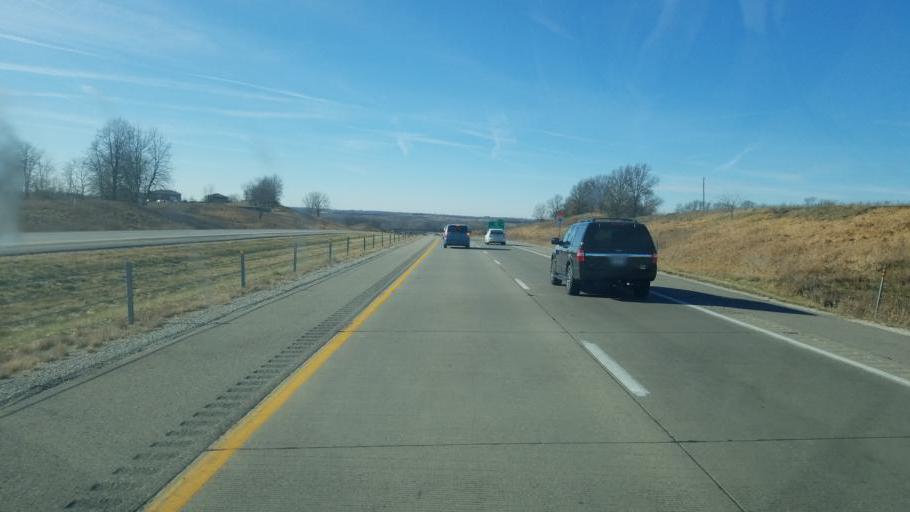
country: US
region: Iowa
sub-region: Dallas County
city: Van Meter
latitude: 41.5502
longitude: -93.9449
